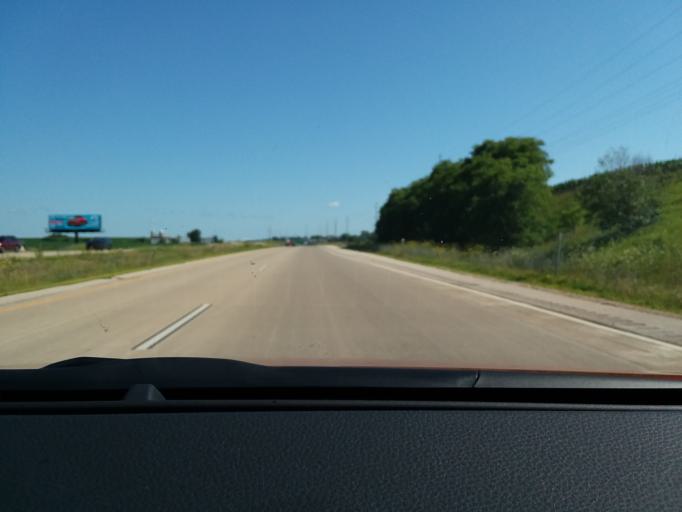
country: US
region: Wisconsin
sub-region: Dane County
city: Windsor
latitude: 43.2005
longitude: -89.3235
